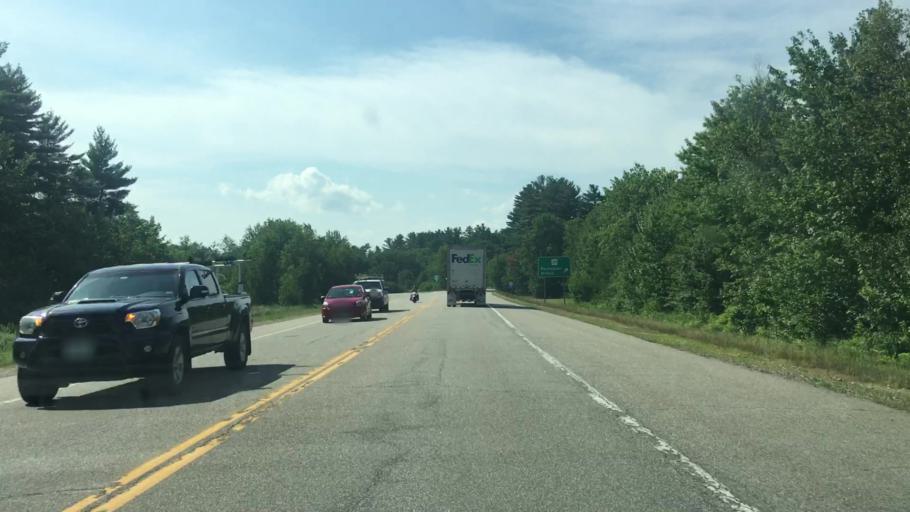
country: US
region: New Hampshire
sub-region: Strafford County
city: Rochester
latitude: 43.3295
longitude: -70.9690
